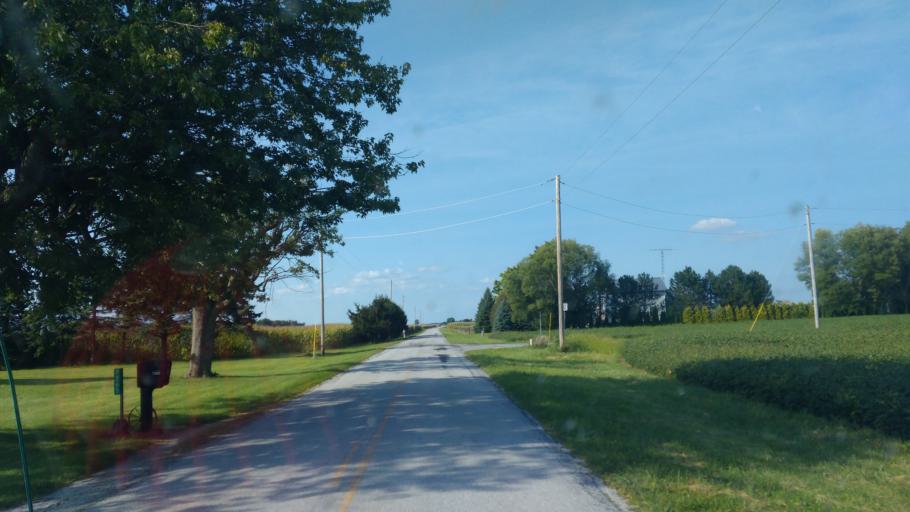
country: US
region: Ohio
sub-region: Hardin County
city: Kenton
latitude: 40.7130
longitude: -83.5725
